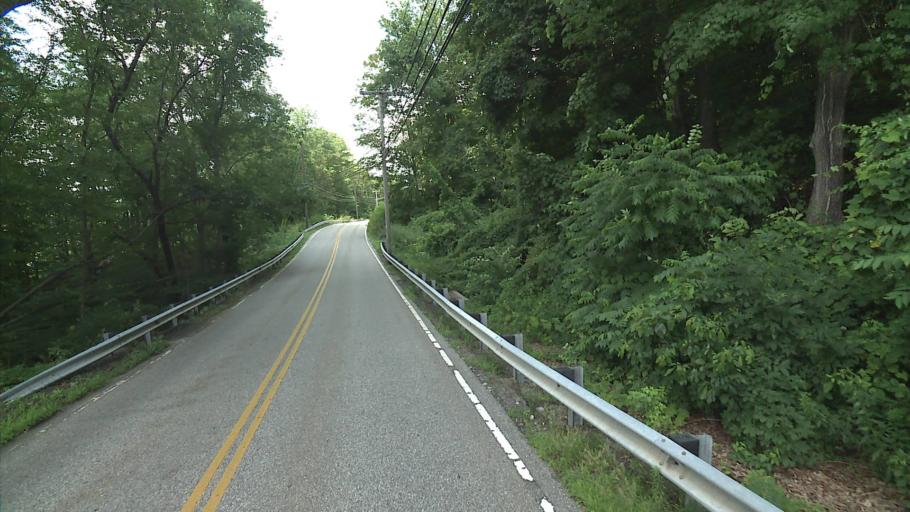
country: US
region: Connecticut
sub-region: New London County
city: Baltic
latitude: 41.6152
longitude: -72.0734
